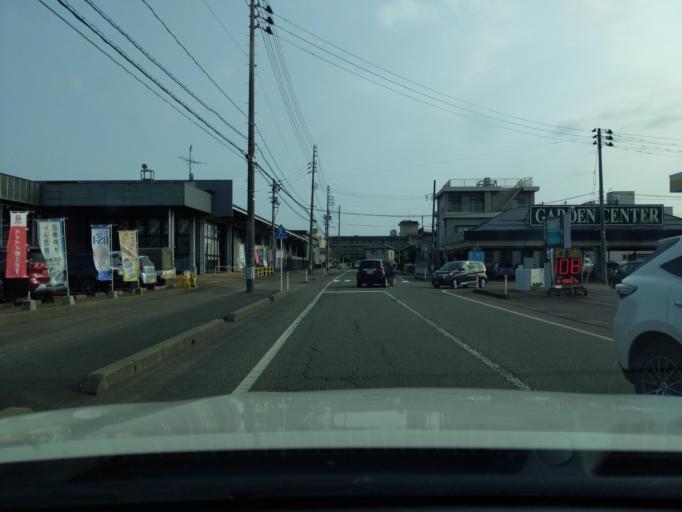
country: JP
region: Niigata
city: Nagaoka
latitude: 37.4532
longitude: 138.8162
